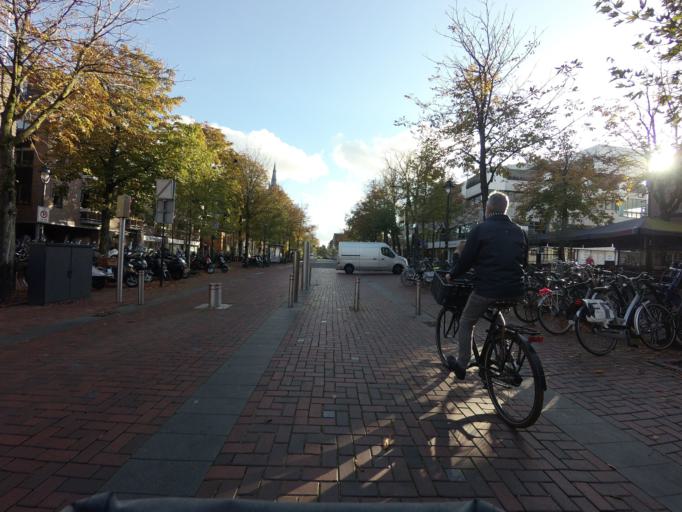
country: NL
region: North Holland
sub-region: Gemeente Hilversum
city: Hilversum
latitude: 52.2244
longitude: 5.1775
